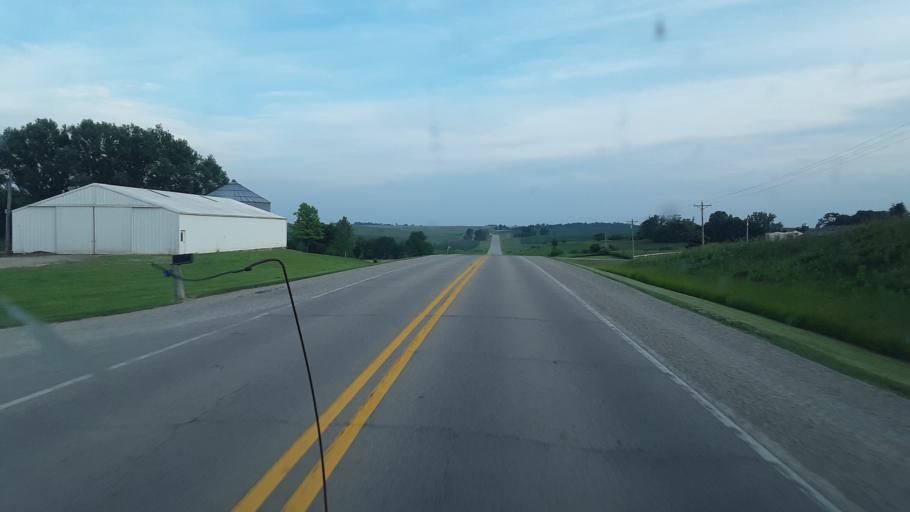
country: US
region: Iowa
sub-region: Benton County
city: Belle Plaine
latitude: 41.7900
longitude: -92.2792
